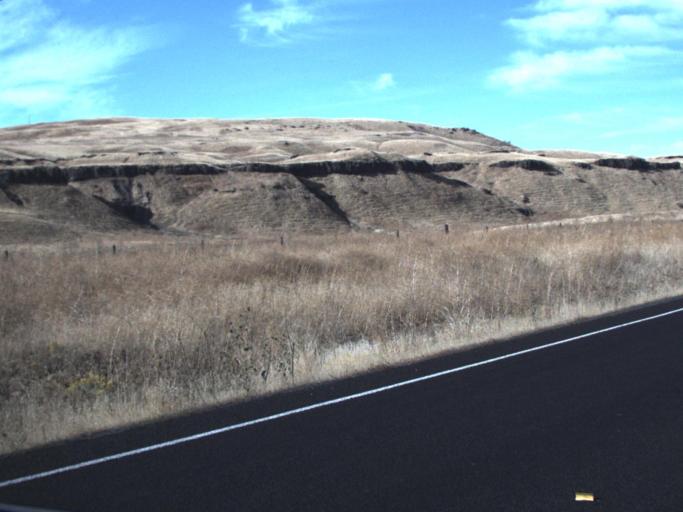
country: US
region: Washington
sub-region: Franklin County
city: Connell
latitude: 46.6451
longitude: -118.5750
